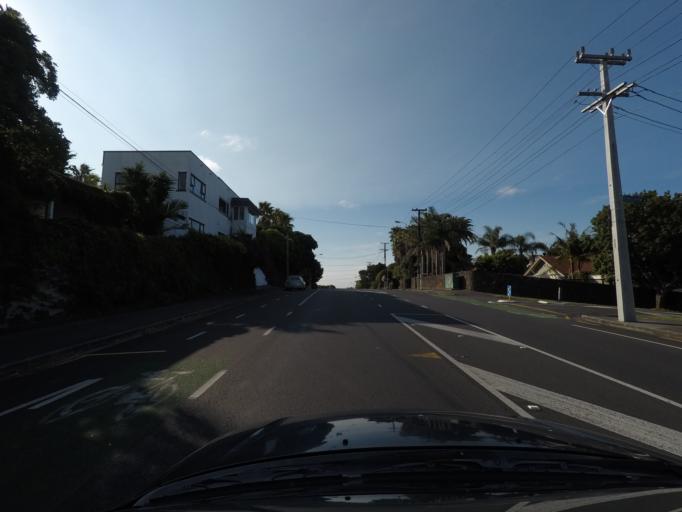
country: NZ
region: Auckland
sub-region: Auckland
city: Auckland
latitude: -36.8869
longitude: 174.7197
